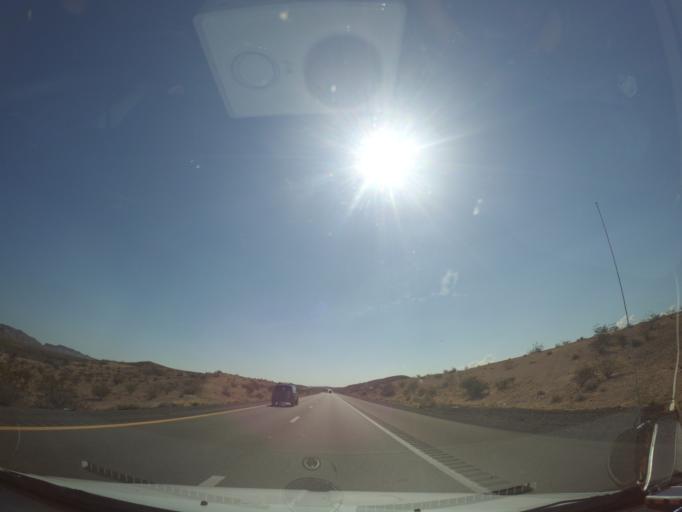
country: US
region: Nevada
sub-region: Clark County
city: Moapa Town
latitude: 36.6130
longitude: -114.6273
